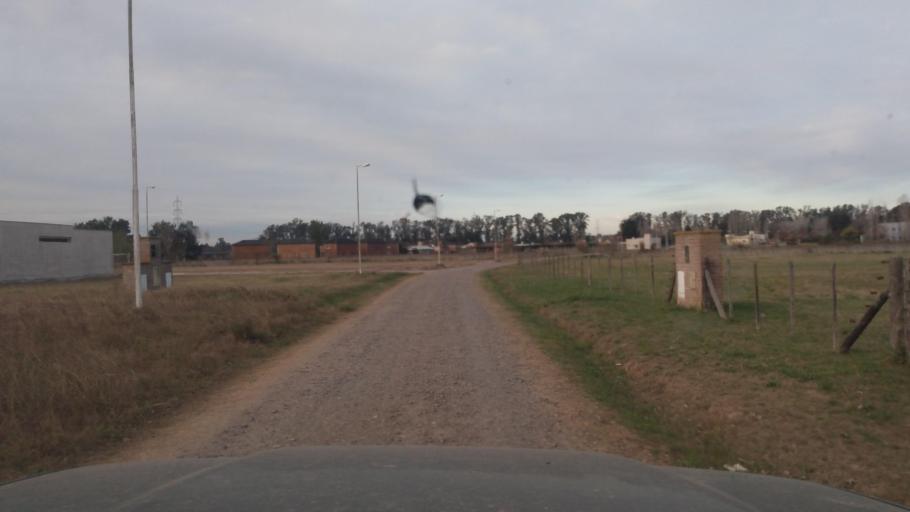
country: AR
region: Buenos Aires
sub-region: Partido de Lujan
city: Lujan
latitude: -34.5755
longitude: -59.0678
